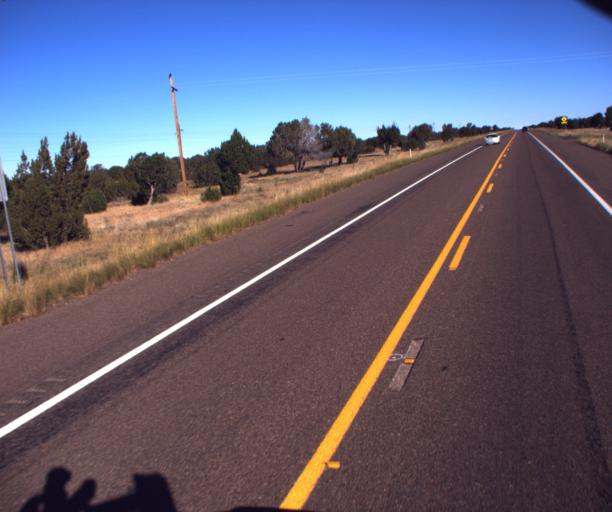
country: US
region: Arizona
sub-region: Navajo County
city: Show Low
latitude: 34.2735
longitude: -110.0244
